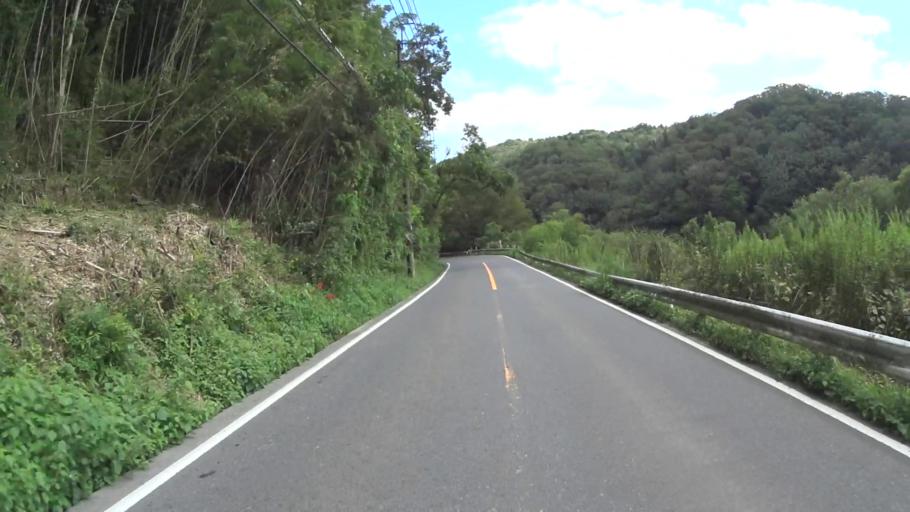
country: JP
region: Kyoto
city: Uji
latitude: 34.9171
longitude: 135.8845
